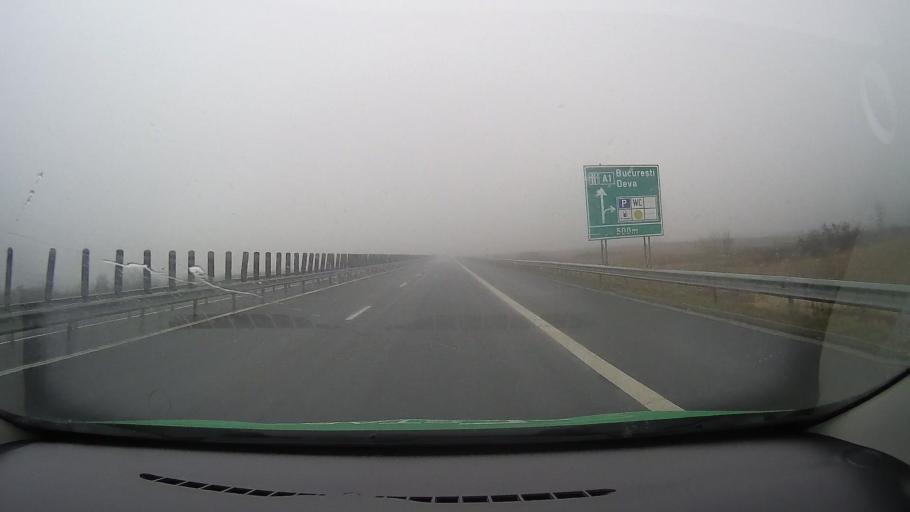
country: RO
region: Timis
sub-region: Comuna Bethausen
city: Bethausen
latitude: 45.8154
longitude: 21.9823
